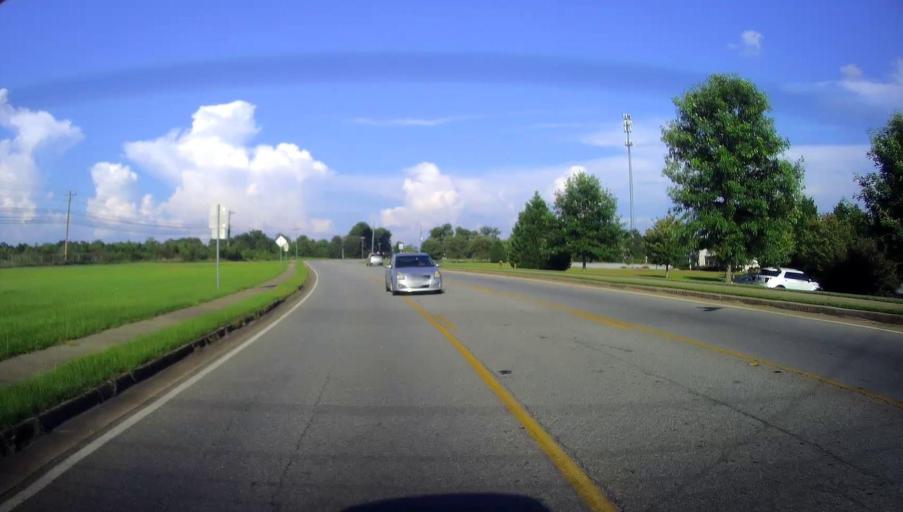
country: US
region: Georgia
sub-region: Houston County
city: Perry
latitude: 32.5057
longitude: -83.6612
